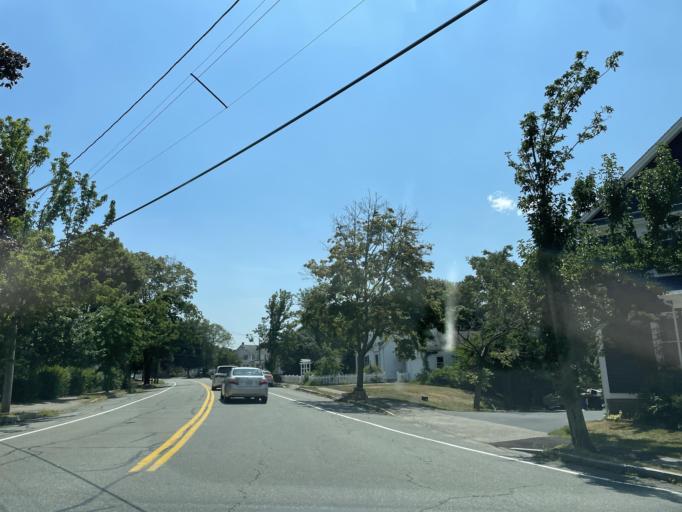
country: US
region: Massachusetts
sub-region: Norfolk County
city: Braintree
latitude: 42.2345
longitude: -71.0023
